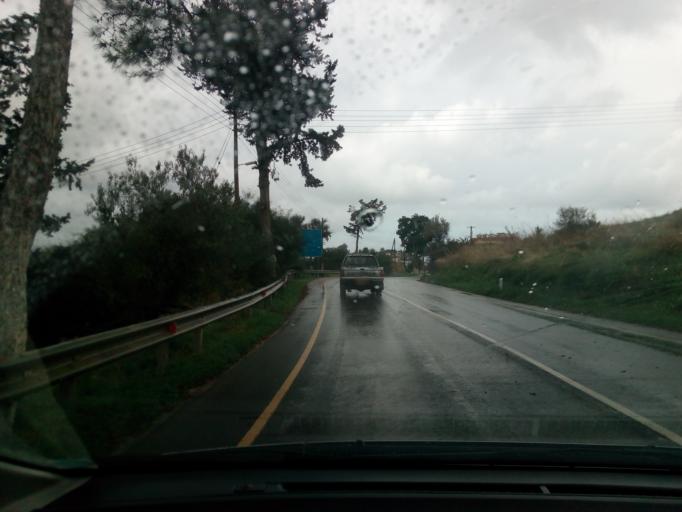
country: CY
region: Pafos
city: Polis
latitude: 35.0248
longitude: 32.4330
